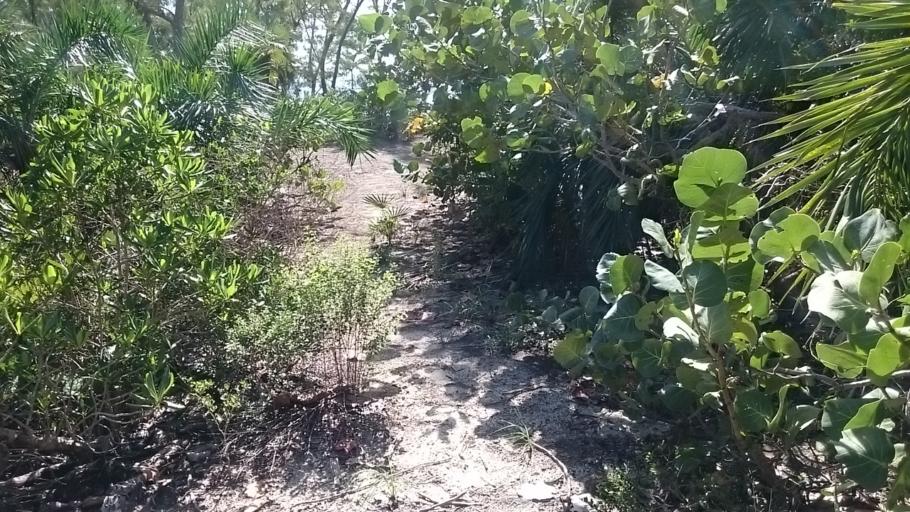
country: BS
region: Cat Island
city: Arthur's Town
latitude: 24.5869
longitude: -75.9634
